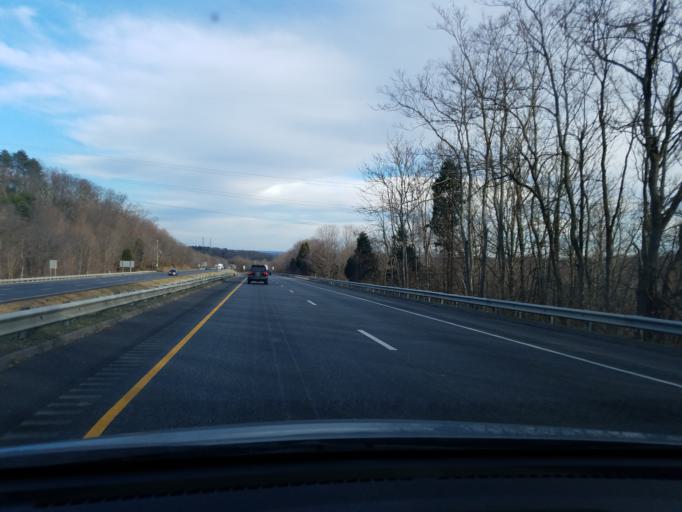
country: US
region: Indiana
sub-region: Floyd County
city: New Albany
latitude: 38.3015
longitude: -85.8614
